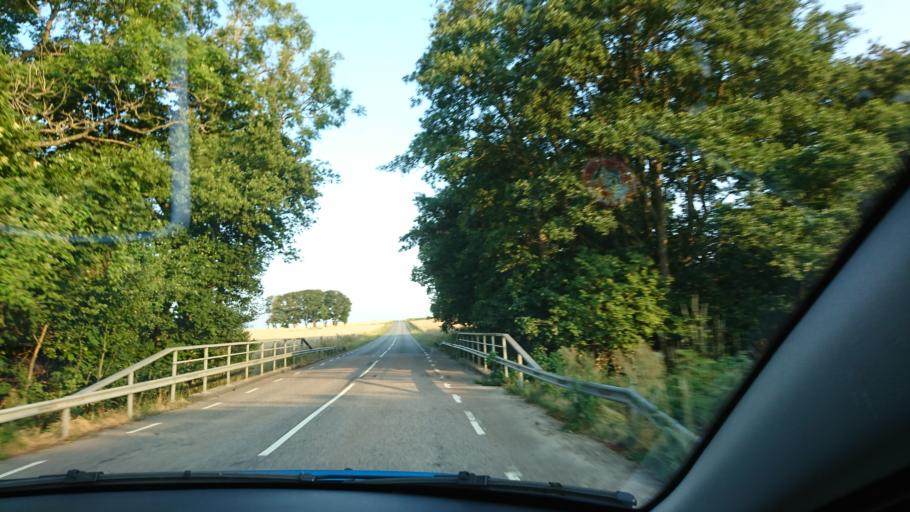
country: SE
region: Skane
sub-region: Simrishamns Kommun
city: Kivik
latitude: 55.7009
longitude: 14.1513
